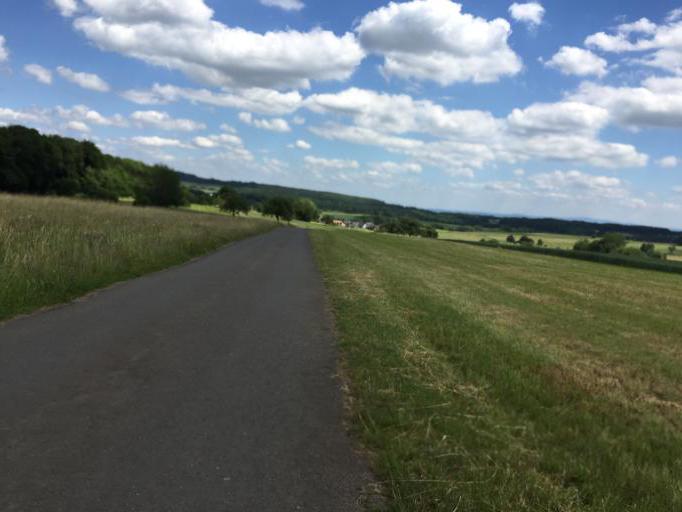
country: DE
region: Rheinland-Pfalz
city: Berod bei Wallmerod
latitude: 50.4765
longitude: 7.9107
